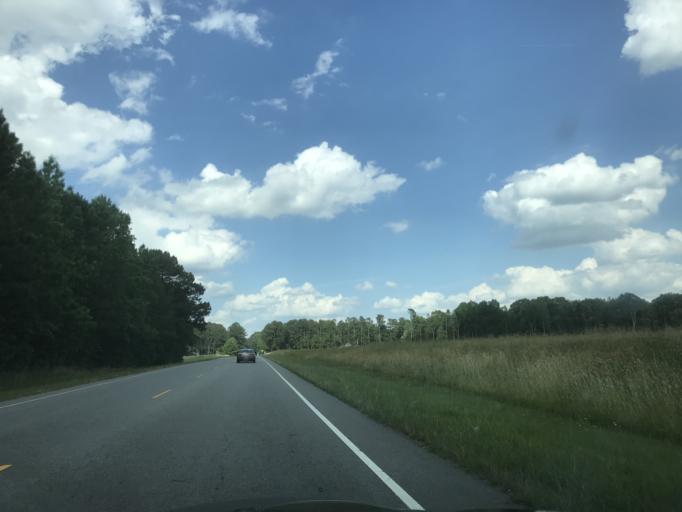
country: US
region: North Carolina
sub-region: Nash County
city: Spring Hope
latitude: 35.9330
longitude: -78.1327
